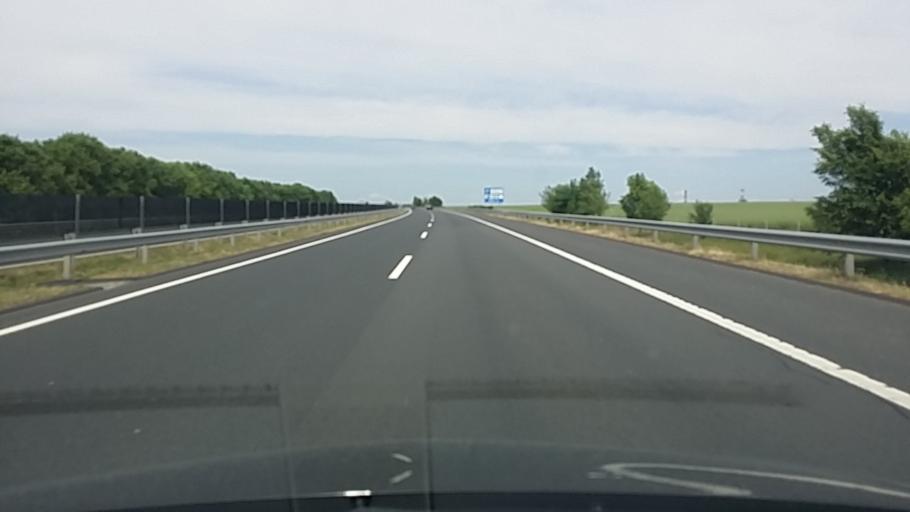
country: HU
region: Fejer
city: Rackeresztur
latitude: 47.2698
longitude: 18.8578
